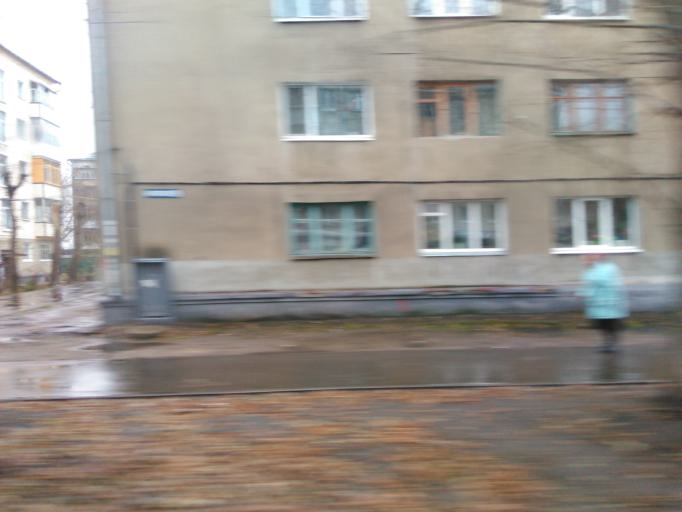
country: RU
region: Tatarstan
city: Osinovo
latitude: 55.8198
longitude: 48.8857
